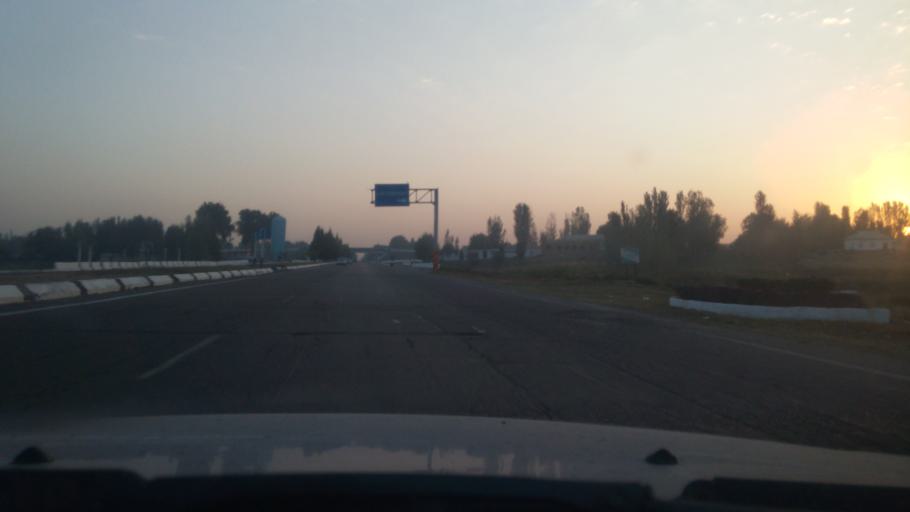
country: UZ
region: Toshkent
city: Amir Timur
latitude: 41.0498
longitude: 68.8945
